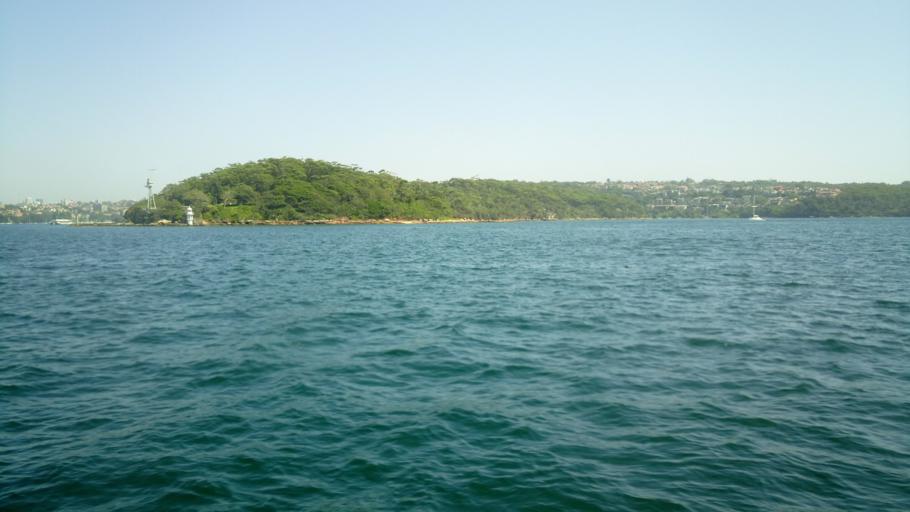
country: AU
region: New South Wales
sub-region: Woollahra
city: Point Piper
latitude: -33.8562
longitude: 151.2499
